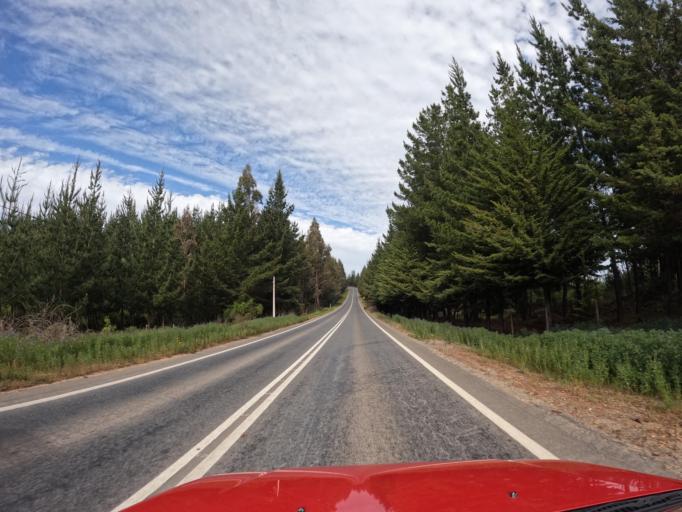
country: CL
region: O'Higgins
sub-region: Provincia de Colchagua
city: Santa Cruz
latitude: -34.3137
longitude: -71.8578
